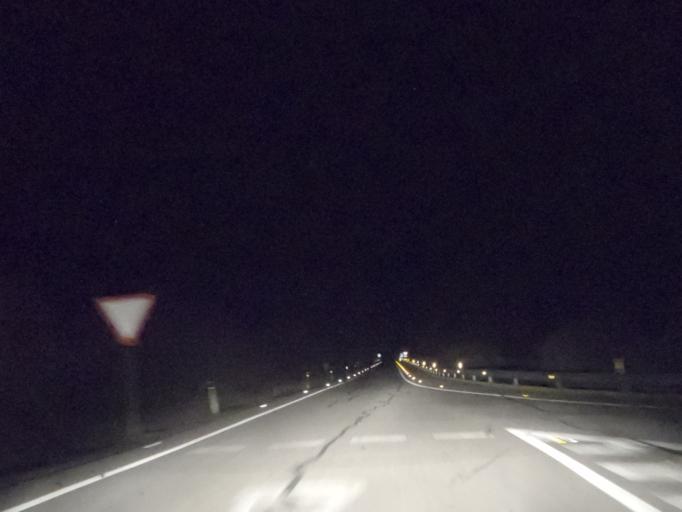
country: ES
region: Castille and Leon
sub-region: Provincia de Zamora
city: Manganeses de la Polvorosa
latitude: 42.0432
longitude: -5.7457
